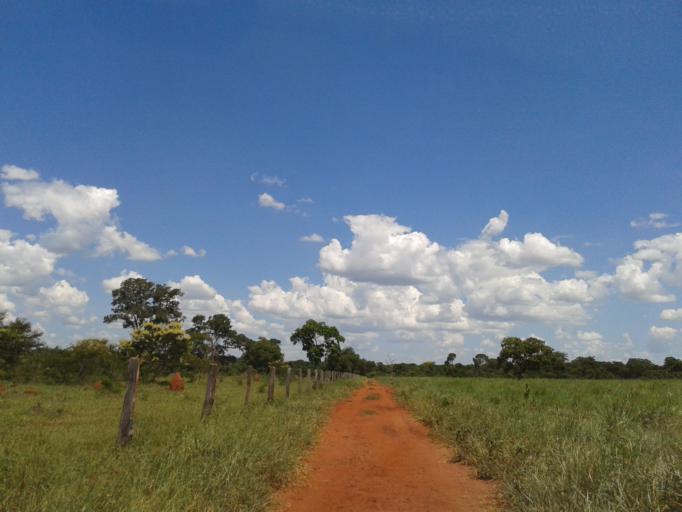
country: BR
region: Minas Gerais
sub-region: Santa Vitoria
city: Santa Vitoria
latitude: -19.1370
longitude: -50.5545
